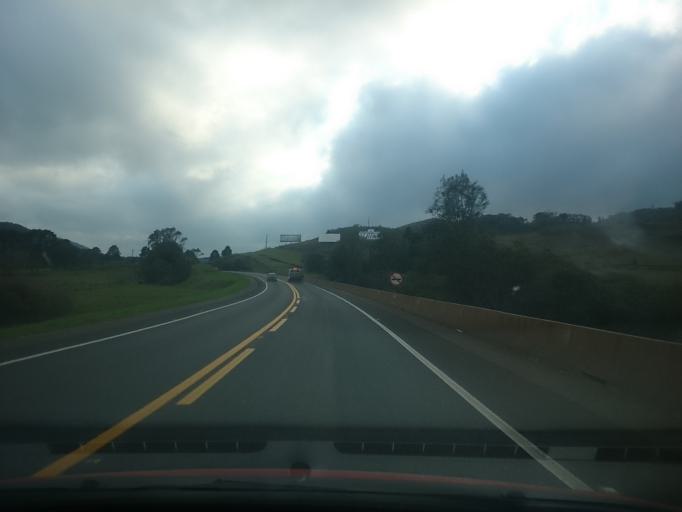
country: BR
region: Santa Catarina
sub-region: Lages
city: Lages
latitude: -27.9279
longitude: -50.4550
